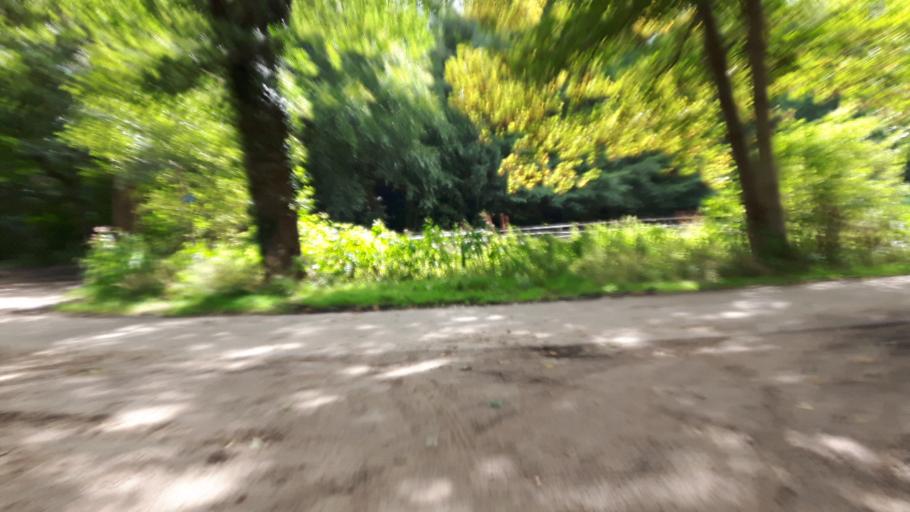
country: NL
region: Groningen
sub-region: Gemeente Haren
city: Haren
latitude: 53.1413
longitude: 6.6161
